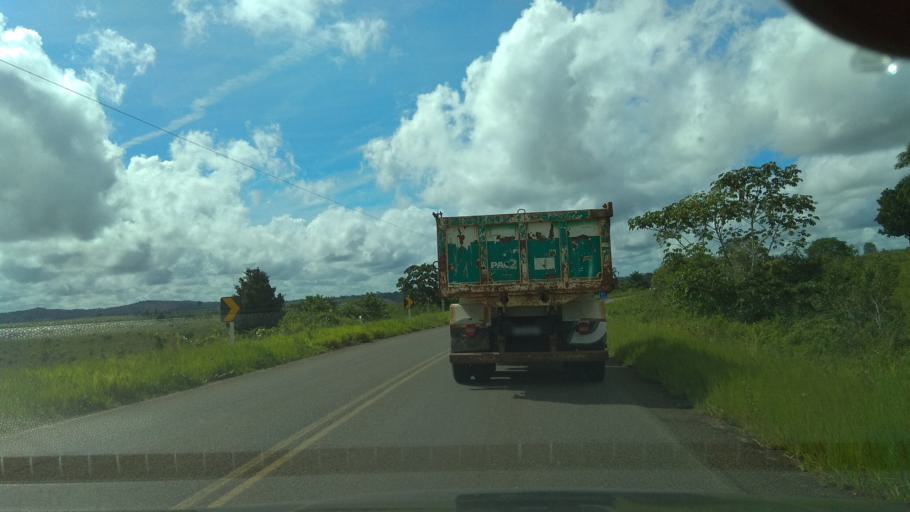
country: BR
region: Bahia
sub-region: Mutuipe
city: Mutuipe
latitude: -13.1649
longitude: -39.3303
